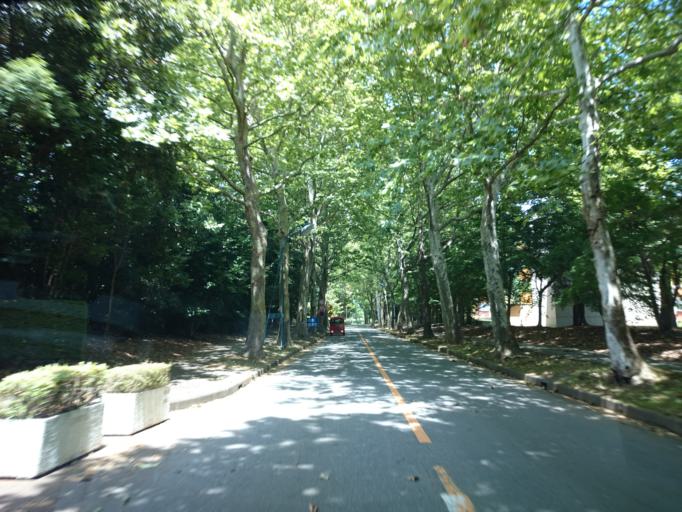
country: JP
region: Ibaraki
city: Tsukuba
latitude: 36.1196
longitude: 140.0965
